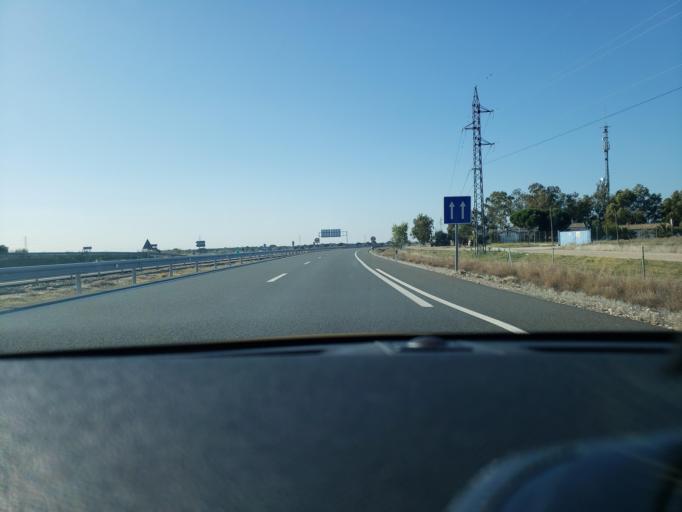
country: ES
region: Castille-La Mancha
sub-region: Province of Toledo
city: Velada
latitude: 39.9431
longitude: -4.9519
